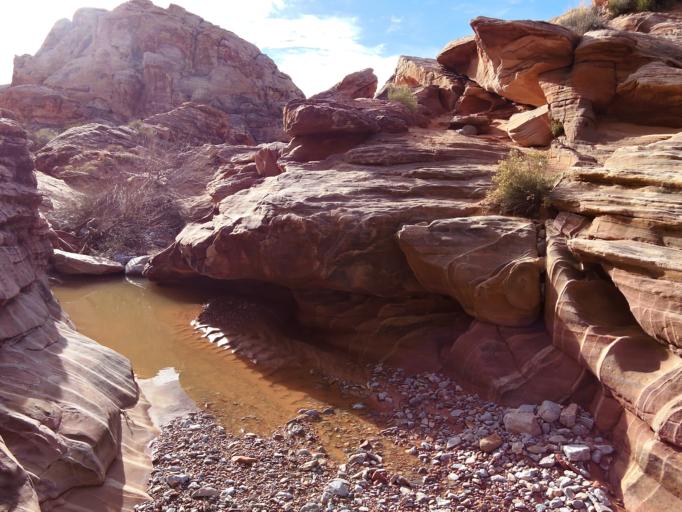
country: US
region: Nevada
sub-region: Clark County
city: Moapa Valley
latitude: 36.4817
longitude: -114.5323
